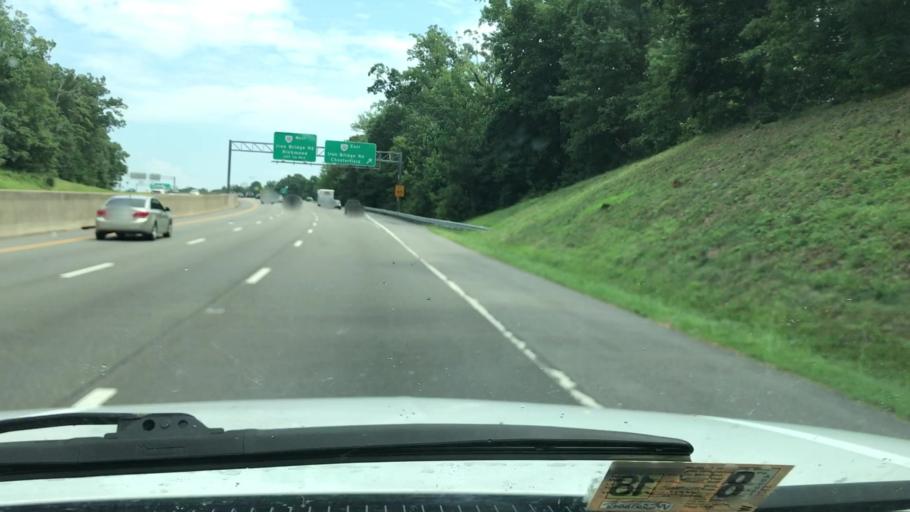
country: US
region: Virginia
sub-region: Chesterfield County
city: Bensley
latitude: 37.4527
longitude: -77.4914
